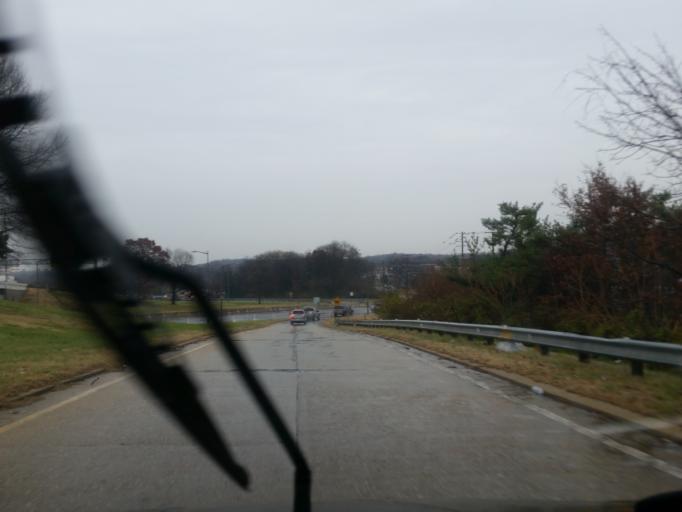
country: US
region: Maryland
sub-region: Prince George's County
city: Silver Hill
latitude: 38.8746
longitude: -76.9754
